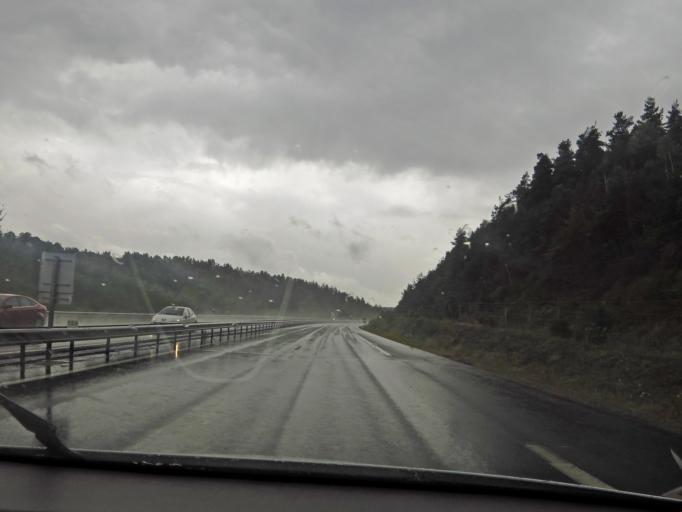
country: FR
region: Auvergne
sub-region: Departement du Cantal
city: Massiac
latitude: 45.1817
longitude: 3.1780
